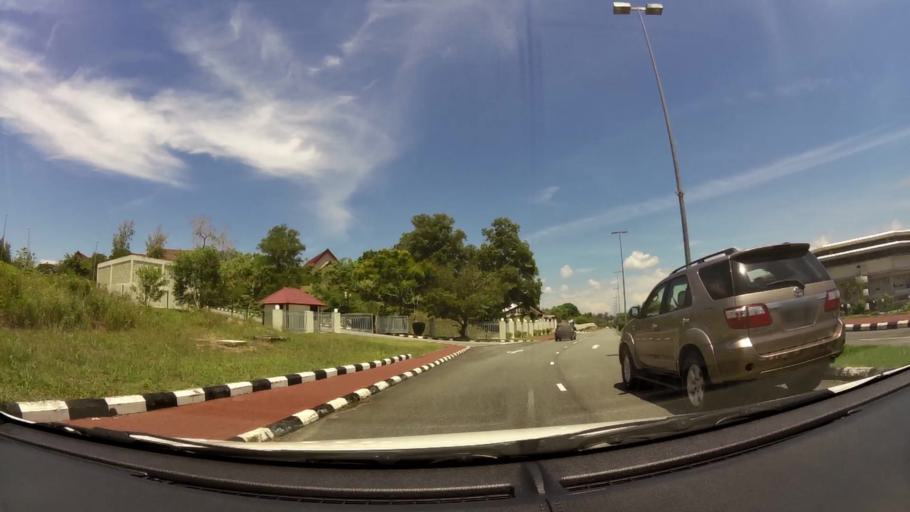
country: BN
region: Brunei and Muara
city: Bandar Seri Begawan
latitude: 4.9264
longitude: 114.9507
